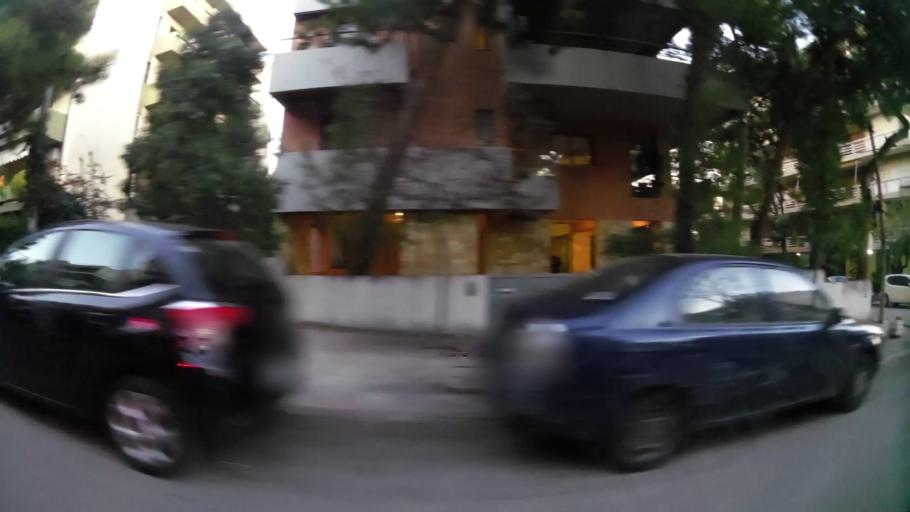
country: GR
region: Attica
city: Pefki
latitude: 38.0614
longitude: 23.8020
